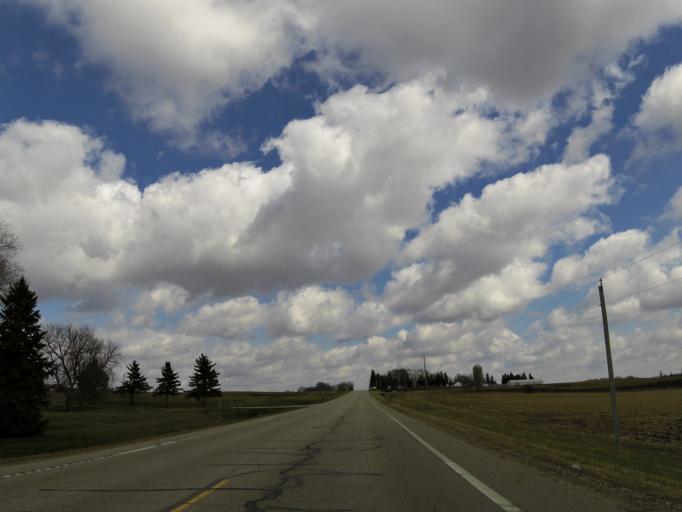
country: US
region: Minnesota
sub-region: Dodge County
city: Mantorville
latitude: 44.0801
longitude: -92.7710
